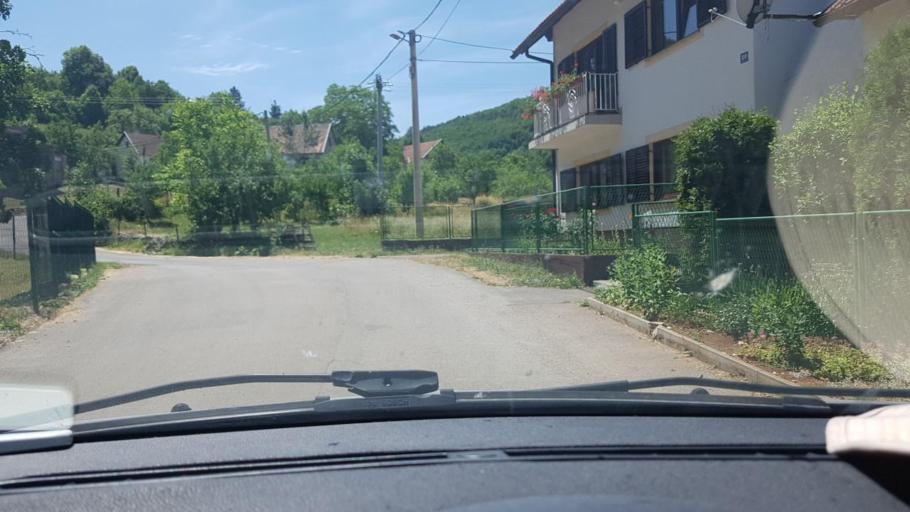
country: HR
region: Licko-Senjska
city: Otocac
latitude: 44.7875
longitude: 15.3664
